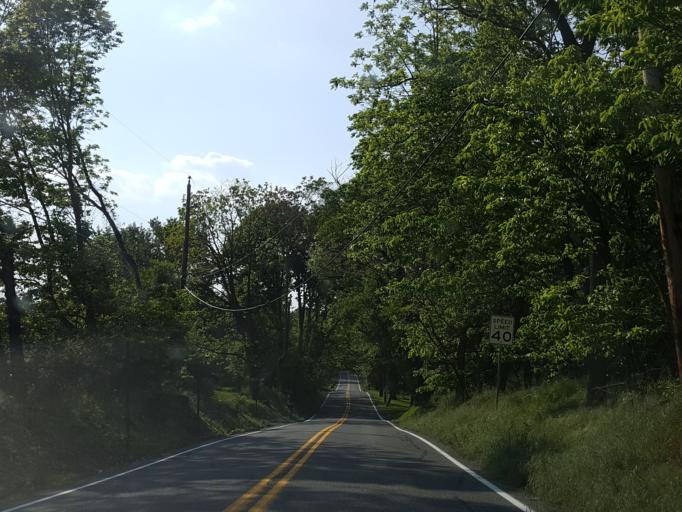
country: US
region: Pennsylvania
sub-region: Lebanon County
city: Campbelltown
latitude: 40.2452
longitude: -76.5984
